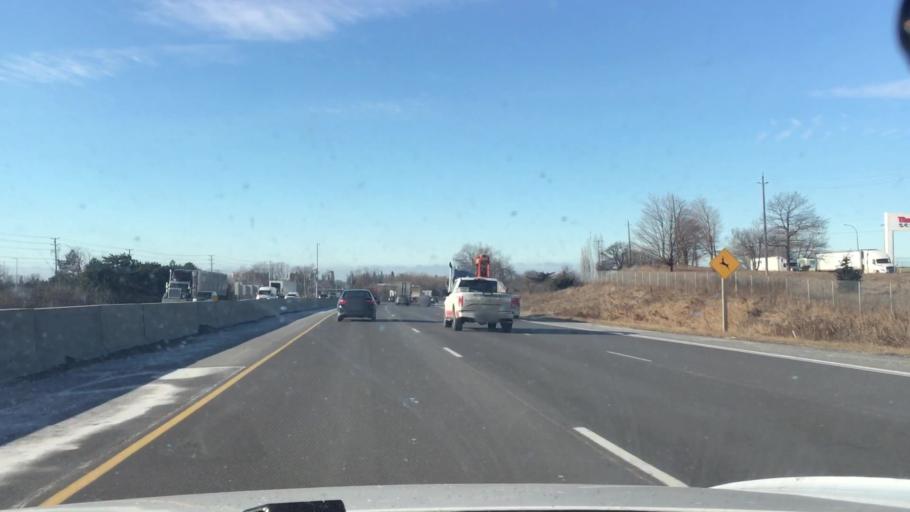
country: CA
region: Ontario
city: Oshawa
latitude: 43.8671
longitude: -78.9174
